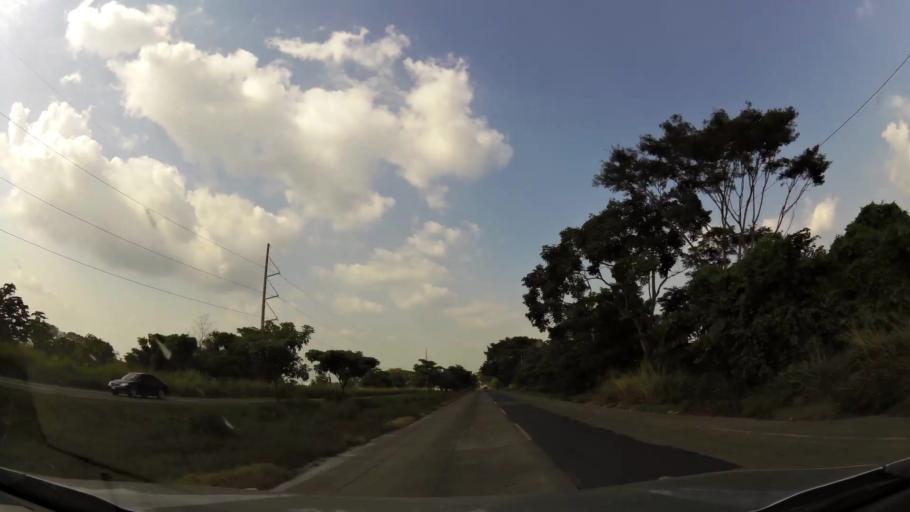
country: GT
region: Escuintla
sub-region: Municipio de Masagua
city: Masagua
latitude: 14.0795
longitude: -90.7779
